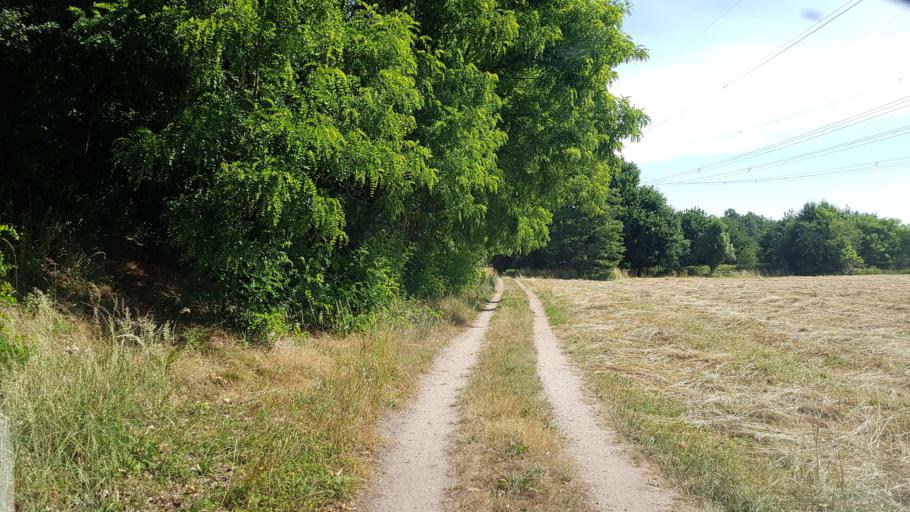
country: DE
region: Brandenburg
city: Altdobern
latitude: 51.6551
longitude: 14.0168
